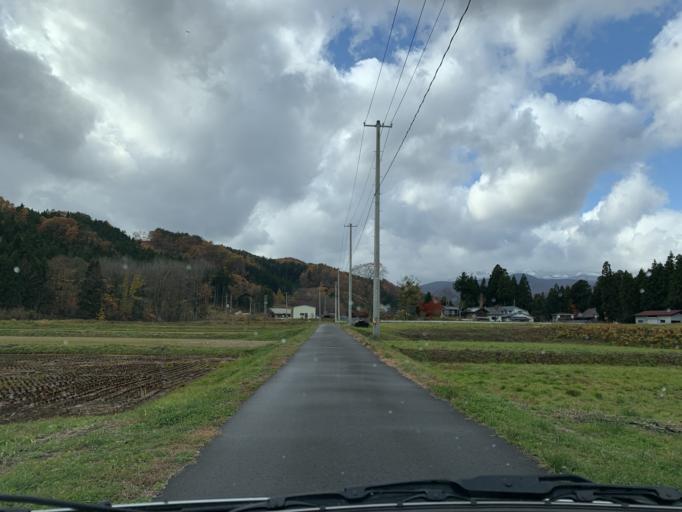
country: JP
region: Iwate
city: Mizusawa
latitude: 39.1155
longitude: 140.9496
